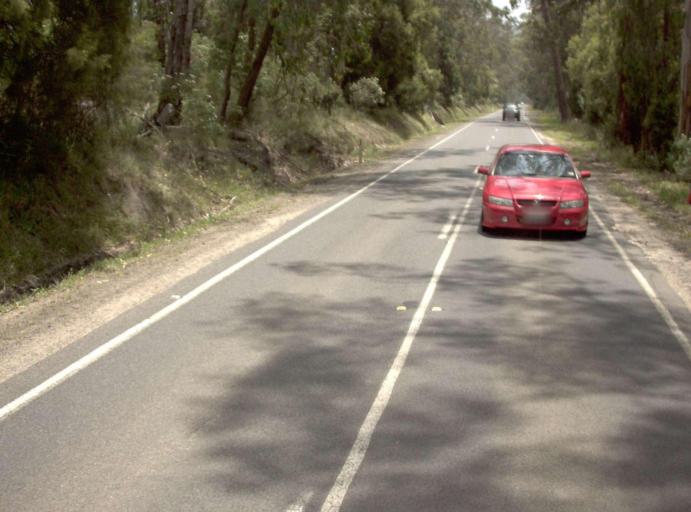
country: AU
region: Victoria
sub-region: Latrobe
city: Traralgon
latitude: -38.4029
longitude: 146.7498
